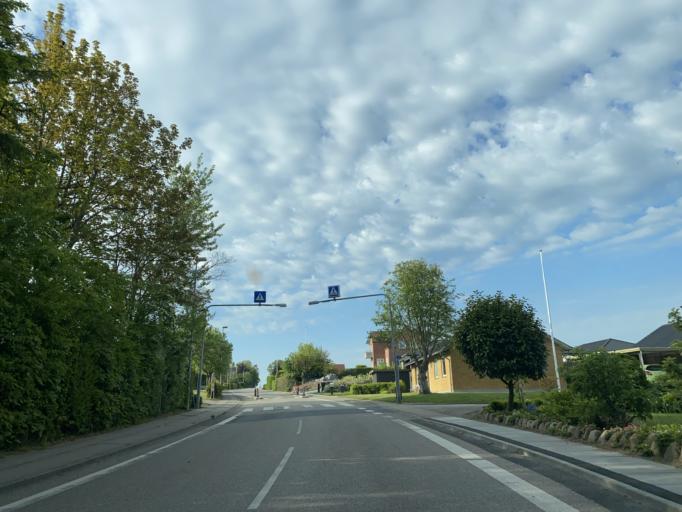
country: DK
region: South Denmark
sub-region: Sonderborg Kommune
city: Dybbol
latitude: 54.9121
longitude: 9.7654
